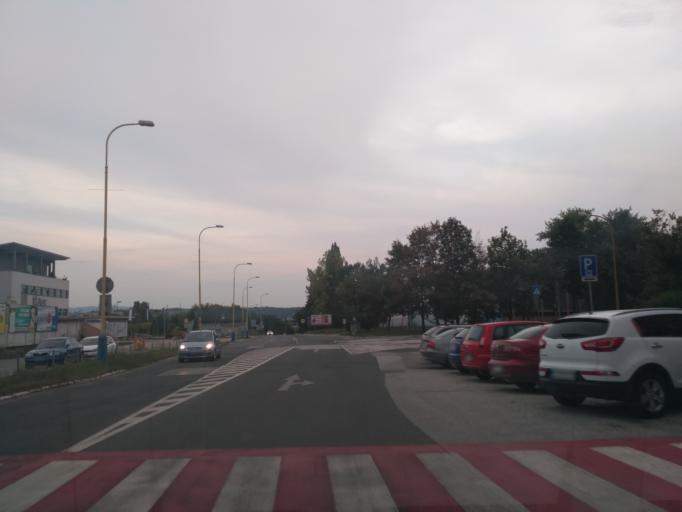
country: SK
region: Kosicky
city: Kosice
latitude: 48.7210
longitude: 21.2386
